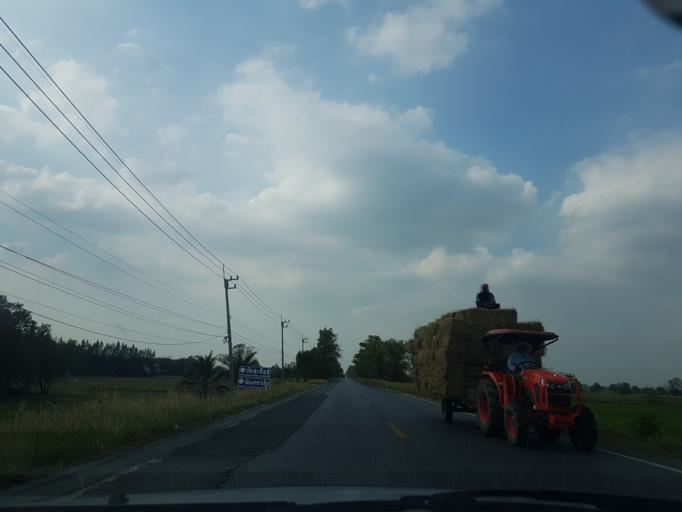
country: TH
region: Phra Nakhon Si Ayutthaya
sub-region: Amphoe Tha Ruea
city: Tha Ruea
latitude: 14.5384
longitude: 100.7420
